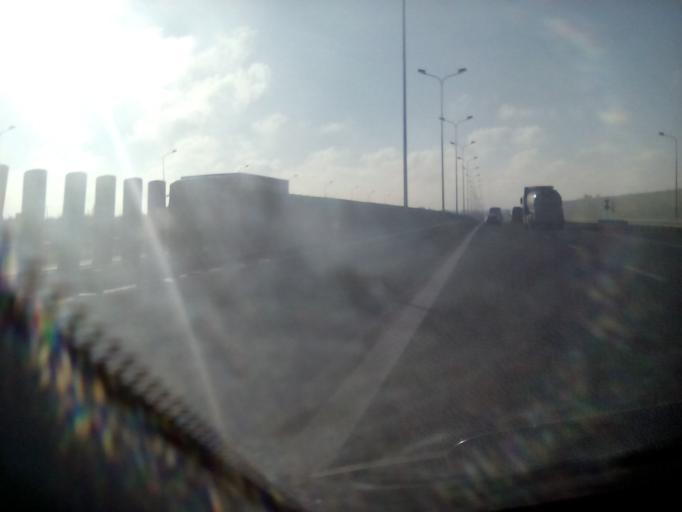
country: PL
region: Masovian Voivodeship
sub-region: Powiat grojecki
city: Grojec
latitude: 51.8265
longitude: 20.8800
